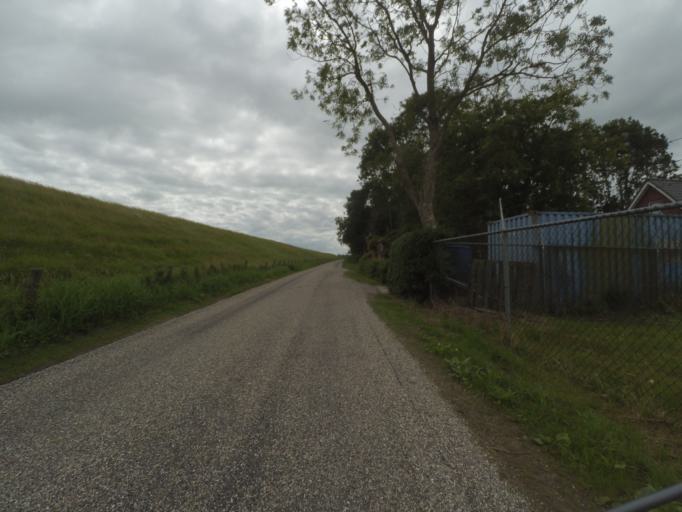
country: NL
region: Friesland
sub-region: Gemeente Dongeradeel
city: Anjum
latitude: 53.3571
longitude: 6.1465
